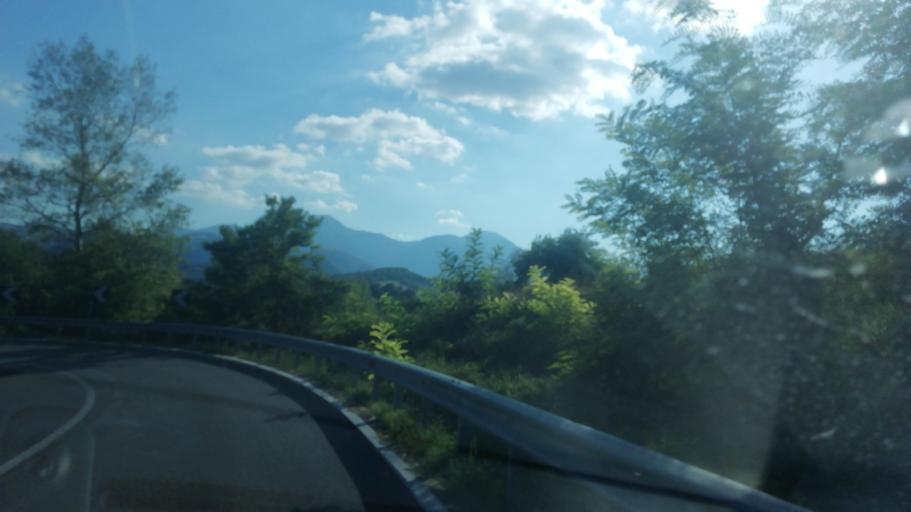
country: IT
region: The Marches
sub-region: Provincia di Pesaro e Urbino
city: Frontone
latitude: 43.5427
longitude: 12.7627
